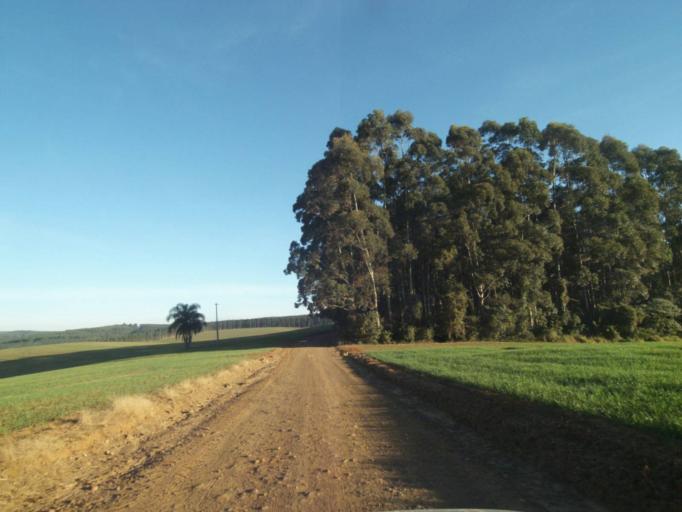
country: BR
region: Parana
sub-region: Telemaco Borba
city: Telemaco Borba
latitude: -24.4767
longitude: -50.5875
